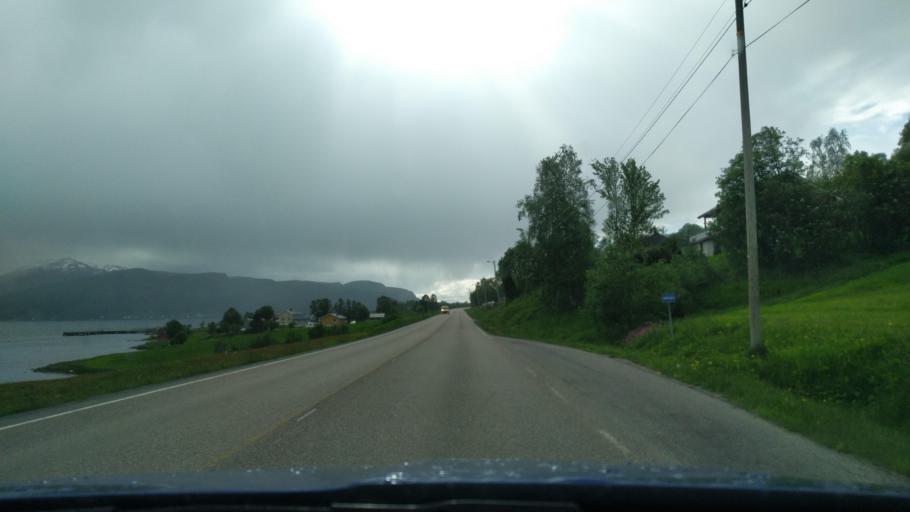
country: NO
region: Troms
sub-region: Sorreisa
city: Sorreisa
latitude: 69.1608
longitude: 18.1391
